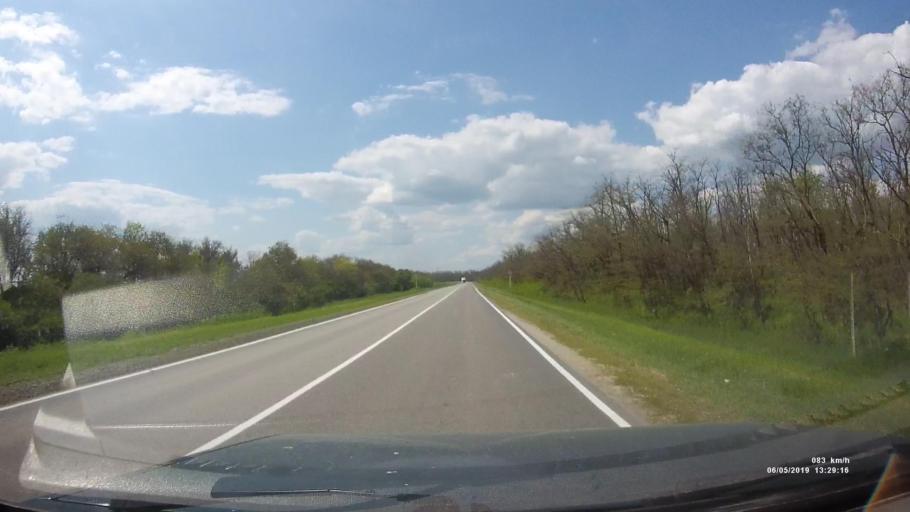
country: RU
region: Rostov
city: Ust'-Donetskiy
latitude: 47.6705
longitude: 40.8475
